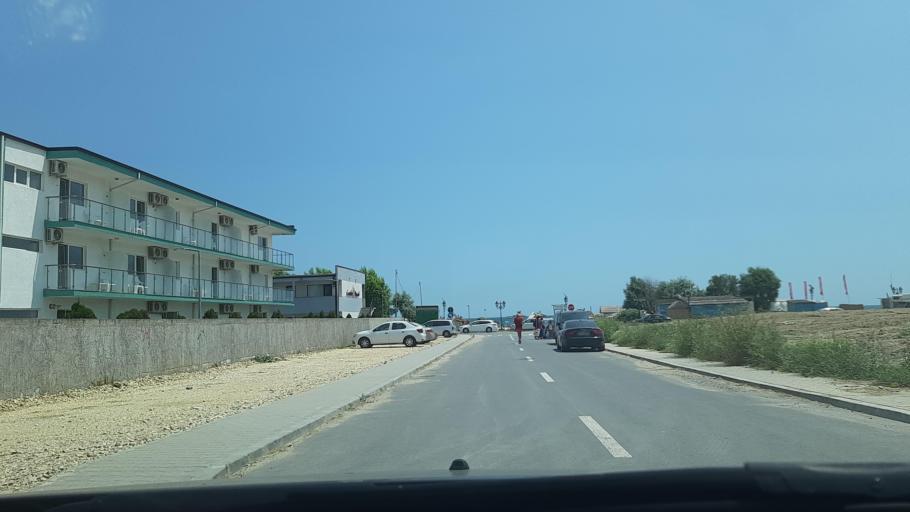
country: RO
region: Constanta
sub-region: Comuna Navodari
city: Navodari
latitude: 44.2966
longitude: 28.6237
